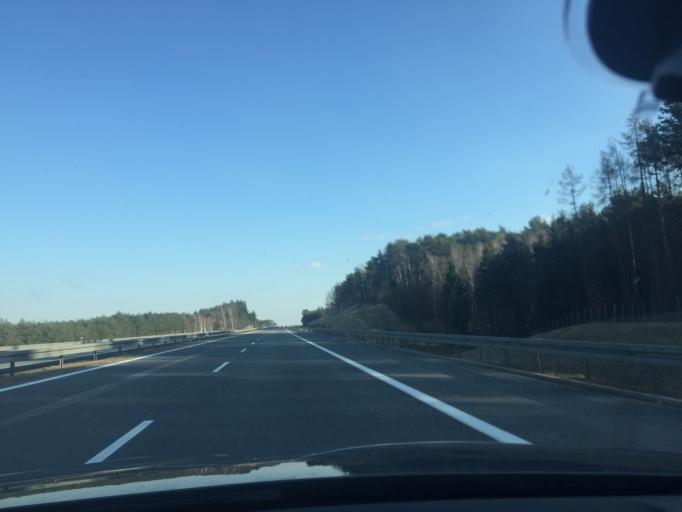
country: PL
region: Lubusz
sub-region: Powiat miedzyrzecki
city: Brojce
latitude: 52.3123
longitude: 15.6080
